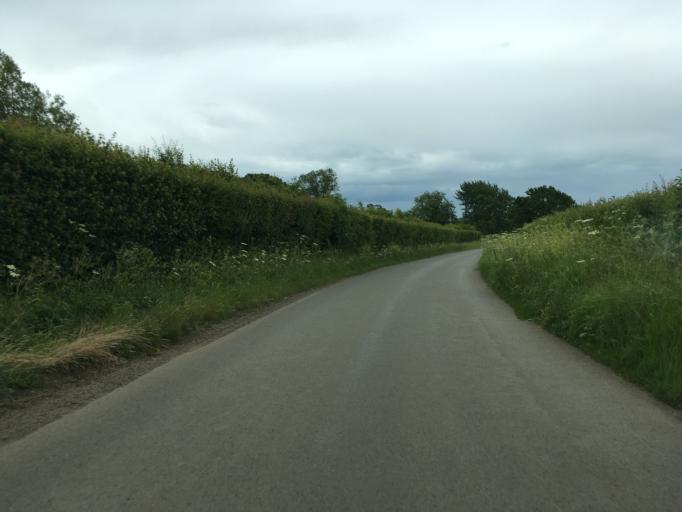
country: GB
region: England
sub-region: Wiltshire
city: Luckington
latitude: 51.5733
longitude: -2.2424
